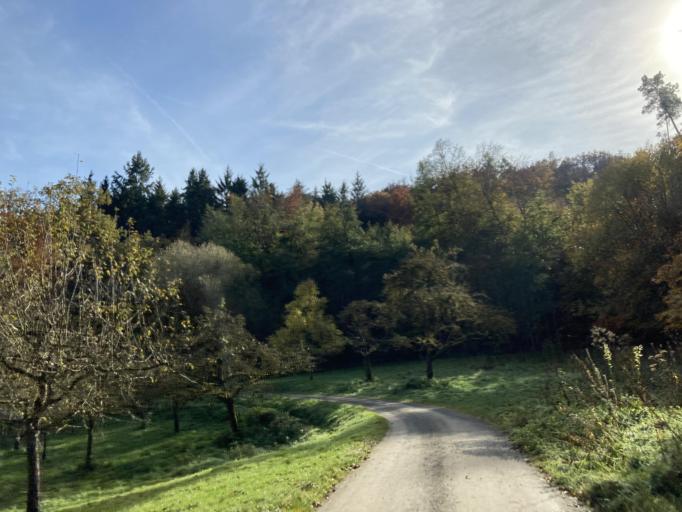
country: DE
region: Baden-Wuerttemberg
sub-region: Tuebingen Region
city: Rottenburg
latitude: 48.4636
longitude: 8.9748
